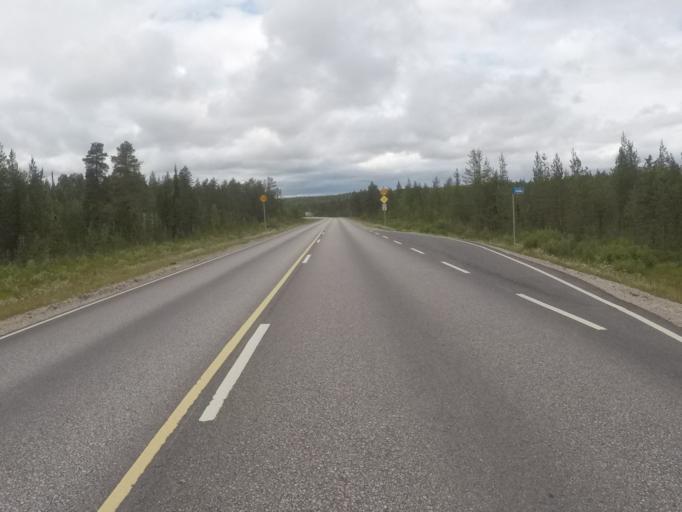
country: FI
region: Lapland
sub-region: Tunturi-Lappi
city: Muonio
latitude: 67.9861
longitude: 23.6452
